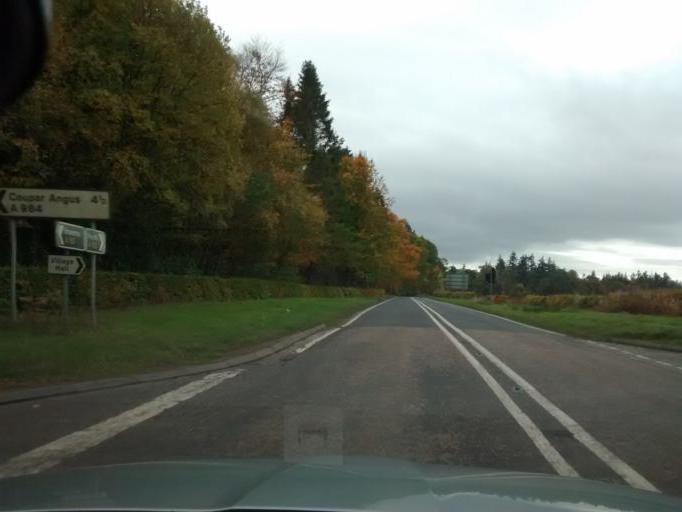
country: GB
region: Scotland
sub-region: Perth and Kinross
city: Blairgowrie
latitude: 56.5401
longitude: -3.3594
